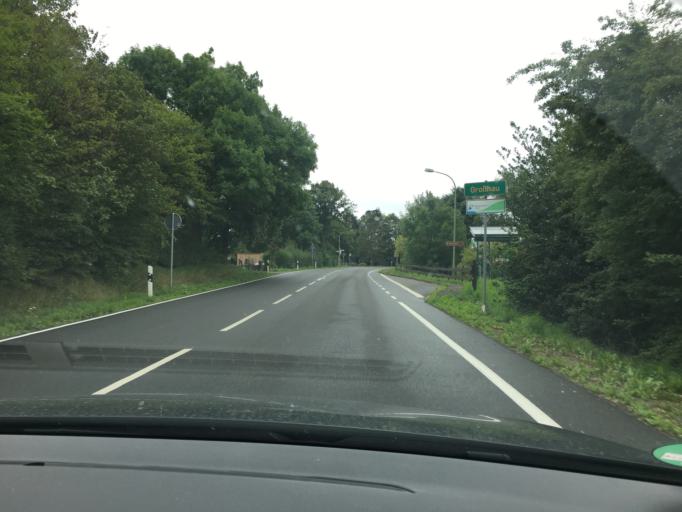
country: DE
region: North Rhine-Westphalia
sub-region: Regierungsbezirk Koln
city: Hurtgenwald
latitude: 50.7365
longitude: 6.3951
